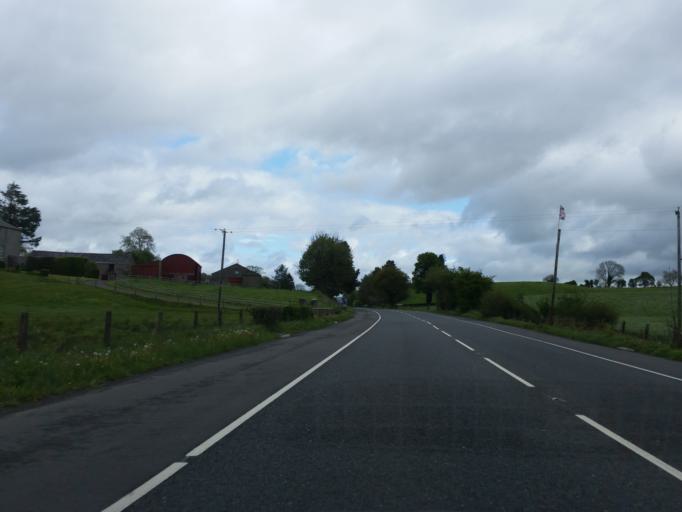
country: GB
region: Northern Ireland
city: Lisnaskea
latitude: 54.3209
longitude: -7.4037
